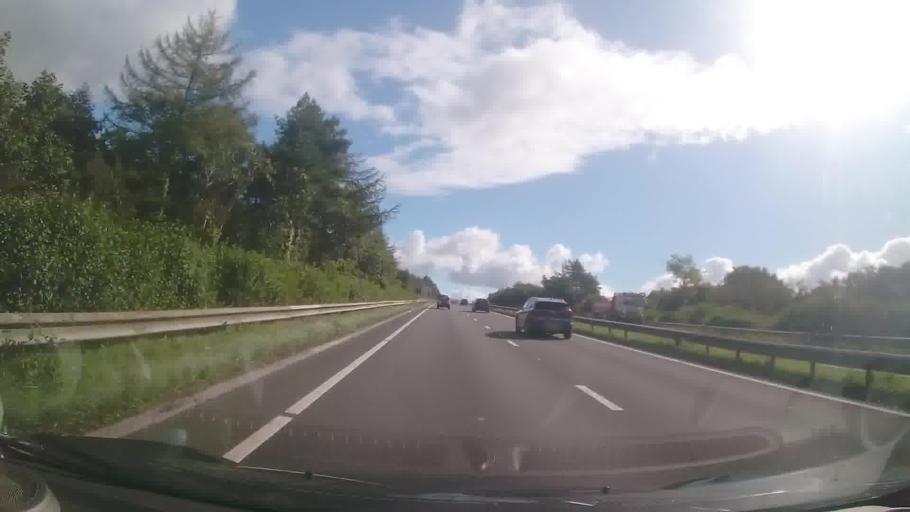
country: GB
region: Wales
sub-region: Carmarthenshire
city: Carmarthen
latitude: 51.8404
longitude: -4.2416
